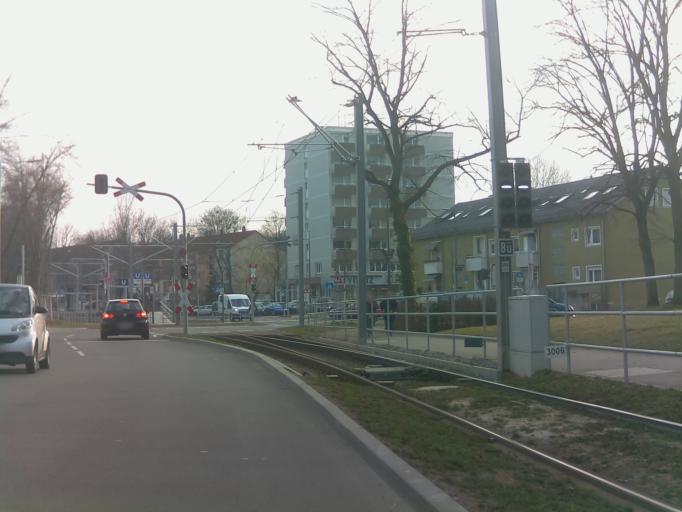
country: DE
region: Baden-Wuerttemberg
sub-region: Regierungsbezirk Stuttgart
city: Steinenbronn
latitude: 48.7203
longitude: 9.1186
